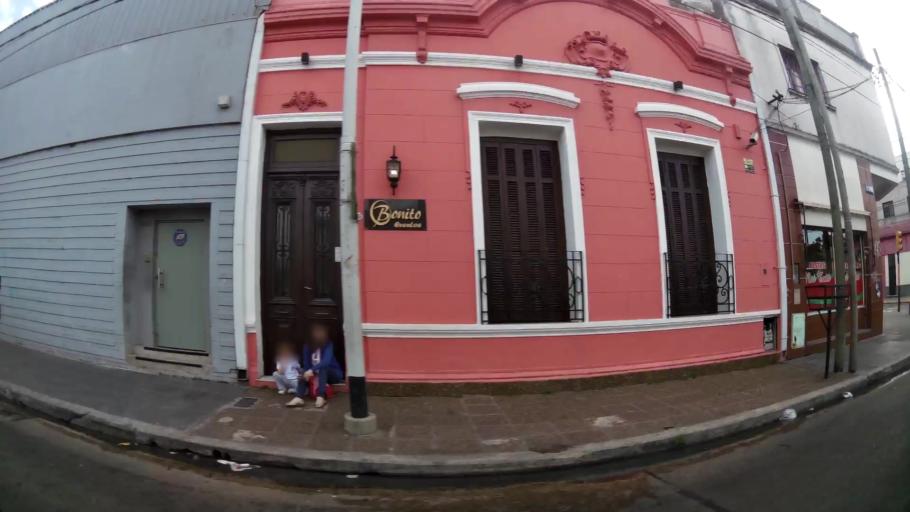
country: AR
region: Buenos Aires
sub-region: Partido de Avellaneda
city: Avellaneda
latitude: -34.6804
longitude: -58.3515
